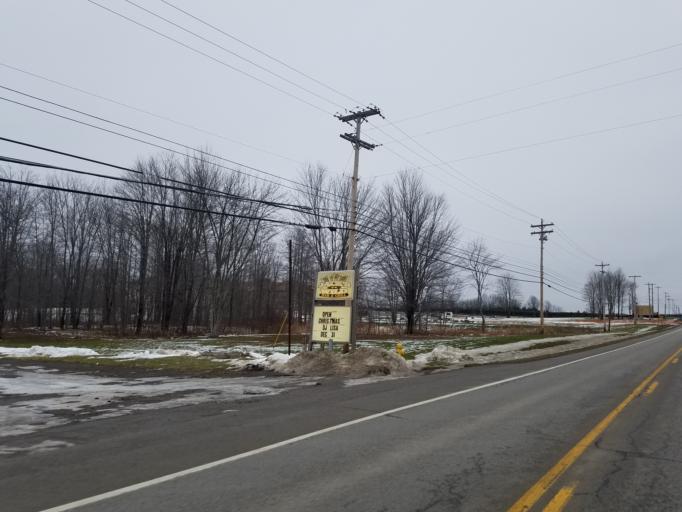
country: US
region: Pennsylvania
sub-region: Mercer County
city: Hermitage
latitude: 41.2375
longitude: -80.3596
